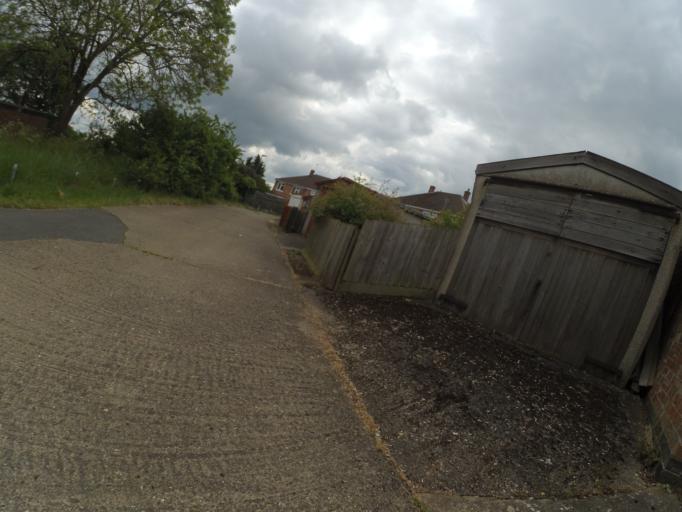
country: GB
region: England
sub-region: Warwickshire
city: Rugby
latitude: 52.3609
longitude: -1.2150
